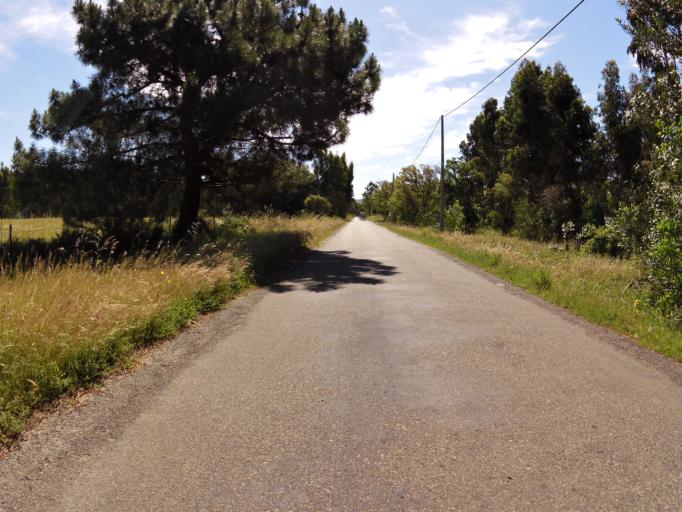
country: PT
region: Setubal
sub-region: Sines
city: Porto Covo
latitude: 37.9371
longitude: -8.7672
